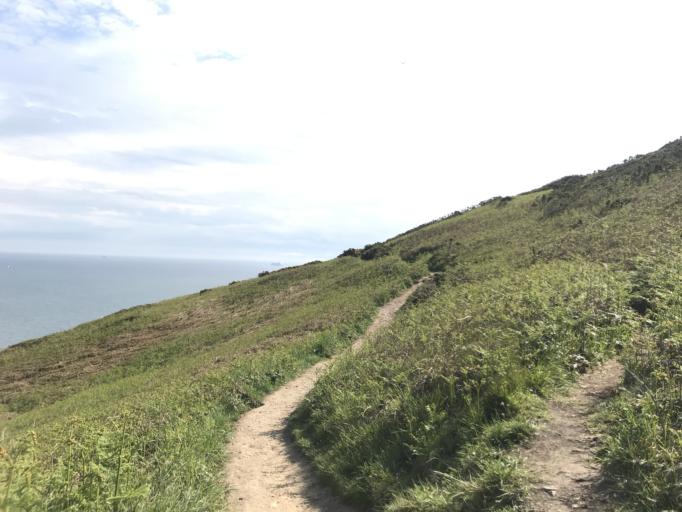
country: IE
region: Leinster
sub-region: Fingal County
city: Howth
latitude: 53.3720
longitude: -6.0507
